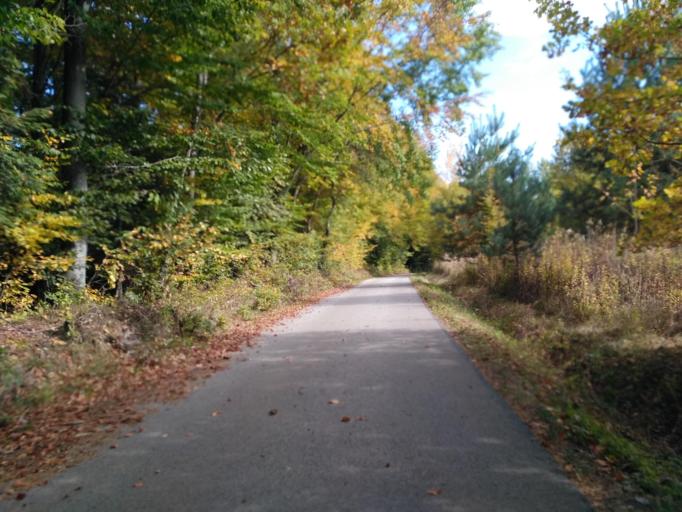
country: PL
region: Subcarpathian Voivodeship
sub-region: Powiat debicki
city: Slotowa
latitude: 49.9254
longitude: 21.2839
